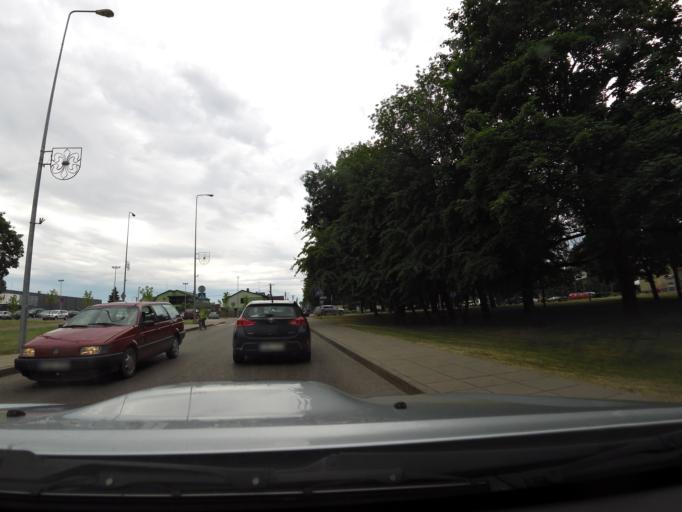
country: LT
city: Vilkaviskis
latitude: 54.6494
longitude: 23.0318
